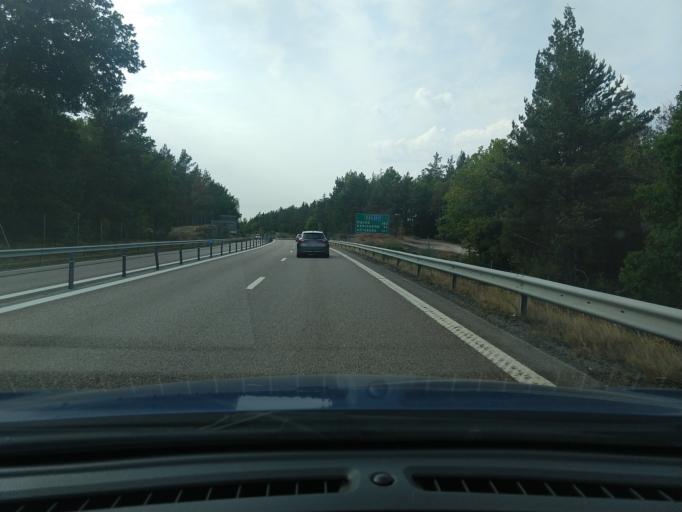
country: SE
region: Blekinge
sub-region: Ronneby Kommun
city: Kallinge
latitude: 56.2117
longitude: 15.3189
